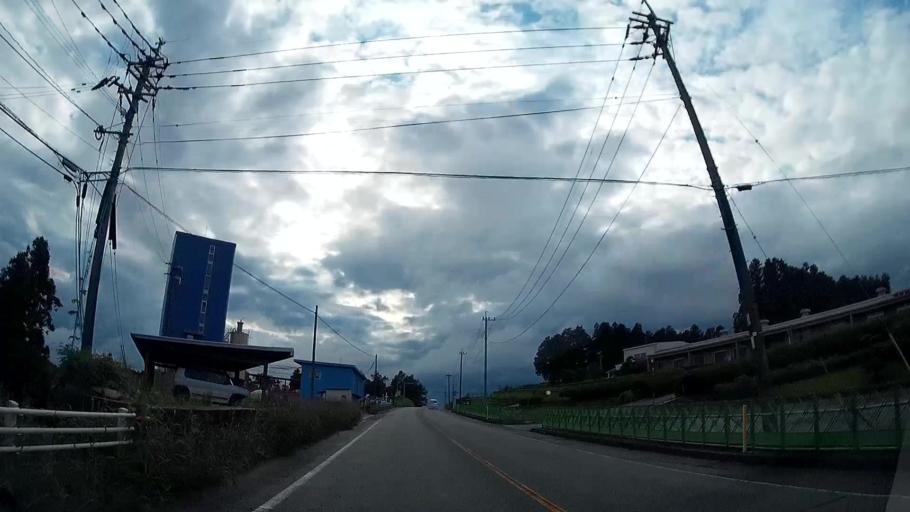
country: JP
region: Kumamoto
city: Ozu
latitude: 32.8776
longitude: 130.9179
